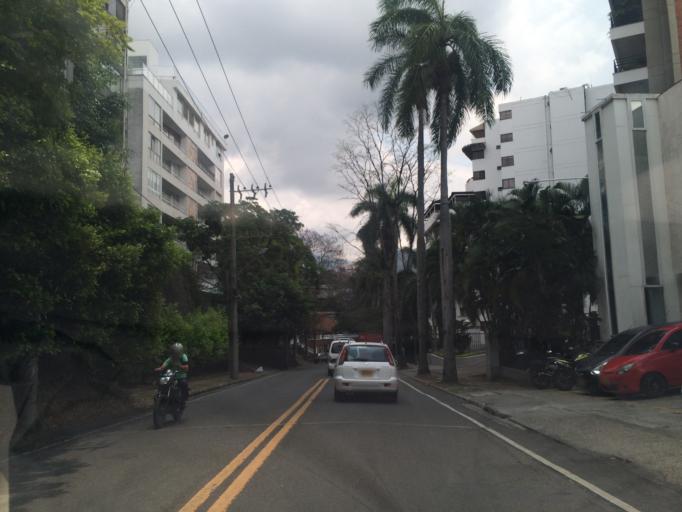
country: CO
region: Valle del Cauca
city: Cali
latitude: 3.4499
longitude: -76.5460
